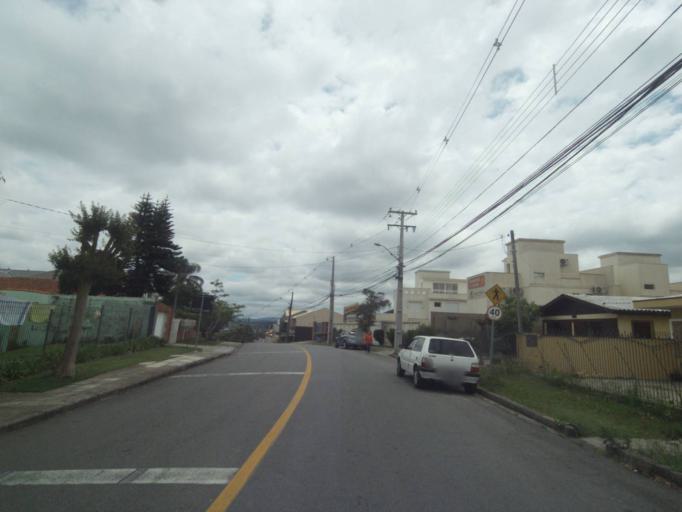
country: BR
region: Parana
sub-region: Curitiba
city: Curitiba
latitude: -25.3931
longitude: -49.2869
